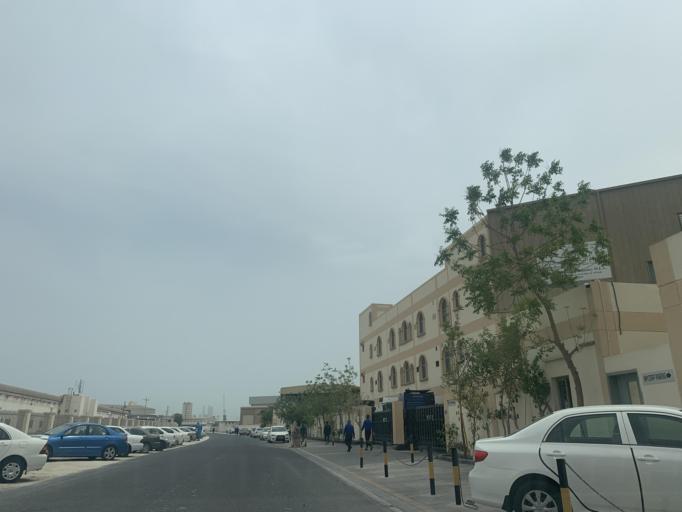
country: BH
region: Muharraq
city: Al Hadd
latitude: 26.2171
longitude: 50.6531
